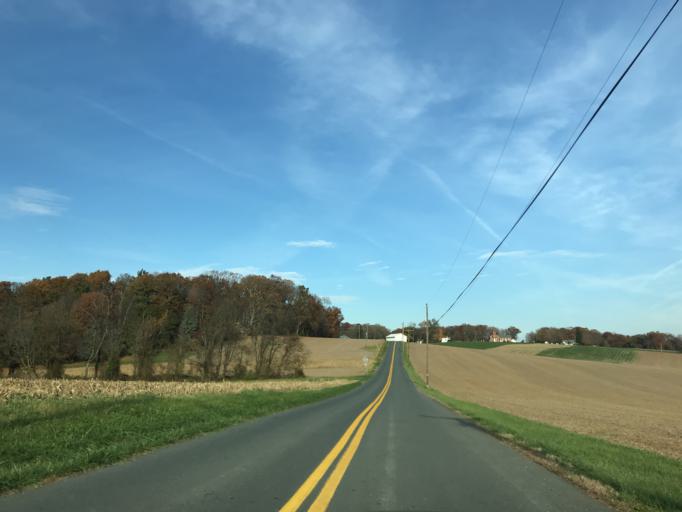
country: US
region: Maryland
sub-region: Carroll County
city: Hampstead
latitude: 39.5711
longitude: -76.7864
